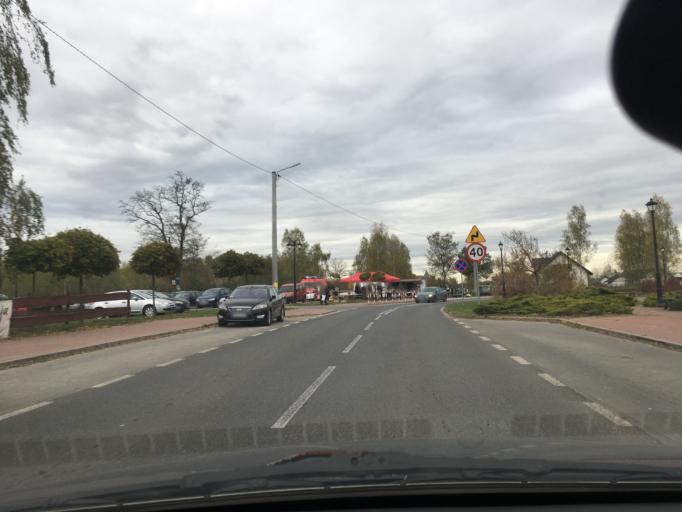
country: PL
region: Lodz Voivodeship
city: Zabia Wola
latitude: 52.0166
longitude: 20.7299
